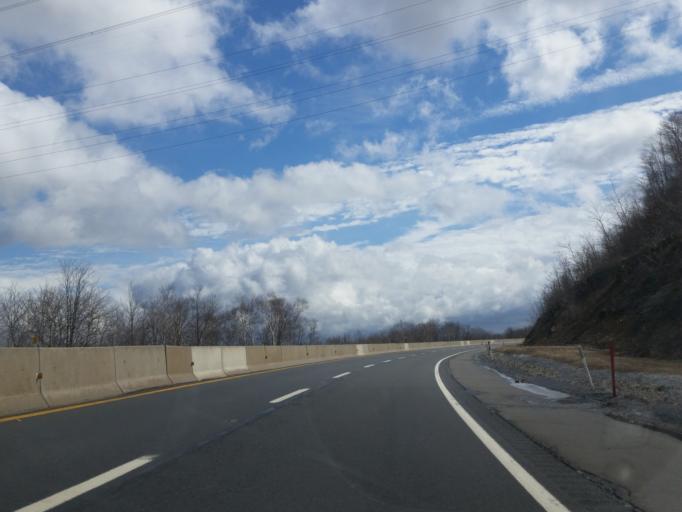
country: US
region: Pennsylvania
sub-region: Lackawanna County
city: Chinchilla
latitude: 41.4594
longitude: -75.6873
